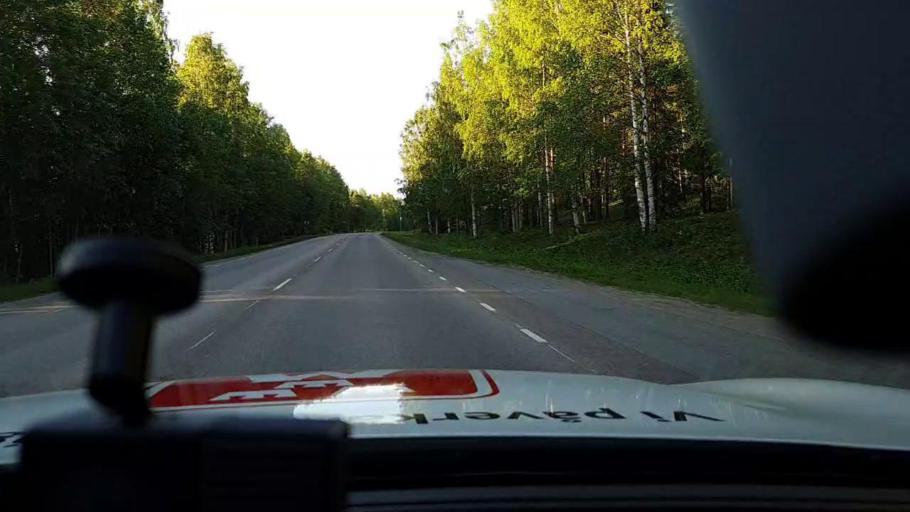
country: SE
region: Norrbotten
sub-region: Lulea Kommun
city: Lulea
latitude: 65.6091
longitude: 22.1877
